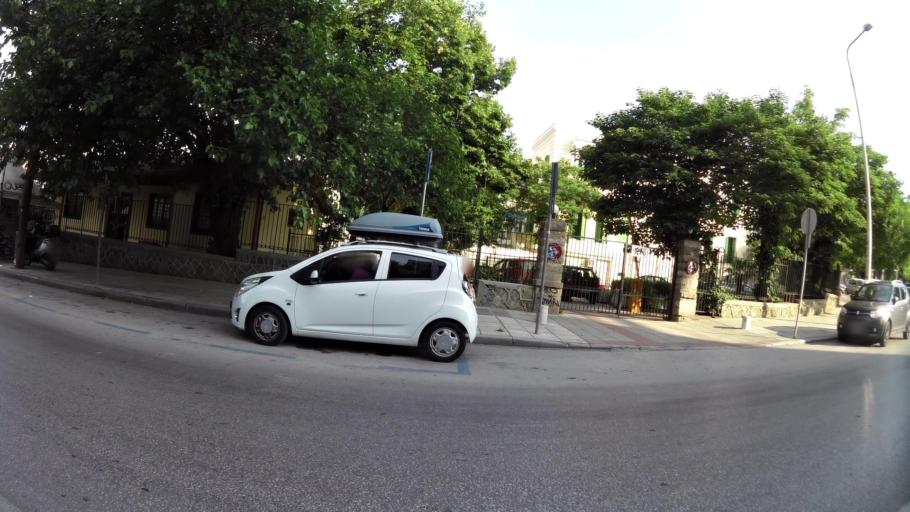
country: GR
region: Central Macedonia
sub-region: Nomos Thessalonikis
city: Agios Pavlos
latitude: 40.6340
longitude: 22.9561
